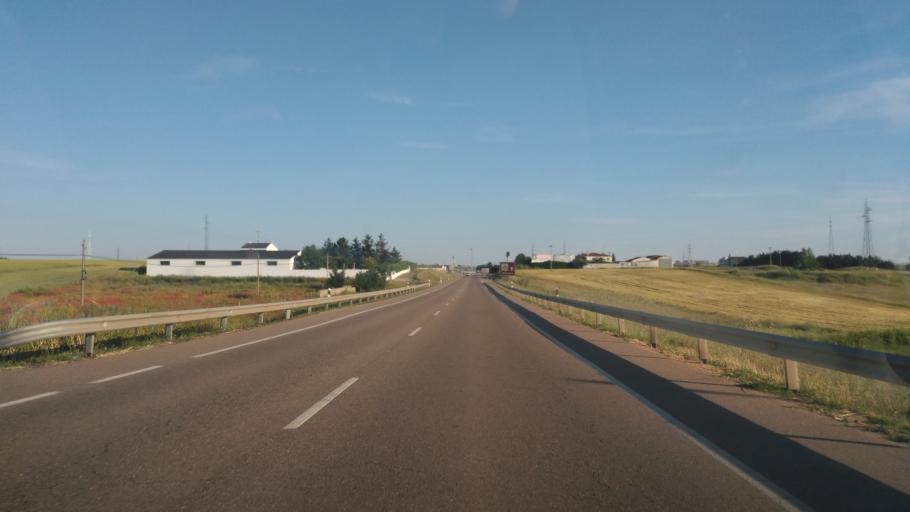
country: ES
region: Castille and Leon
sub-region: Provincia de Salamanca
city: Villares de la Reina
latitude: 41.0075
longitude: -5.6683
